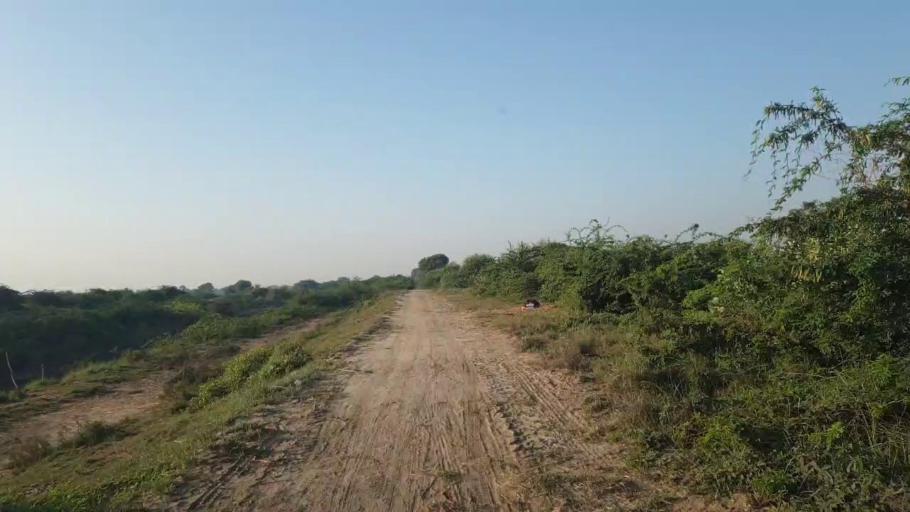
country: PK
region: Sindh
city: Badin
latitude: 24.6125
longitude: 68.7848
